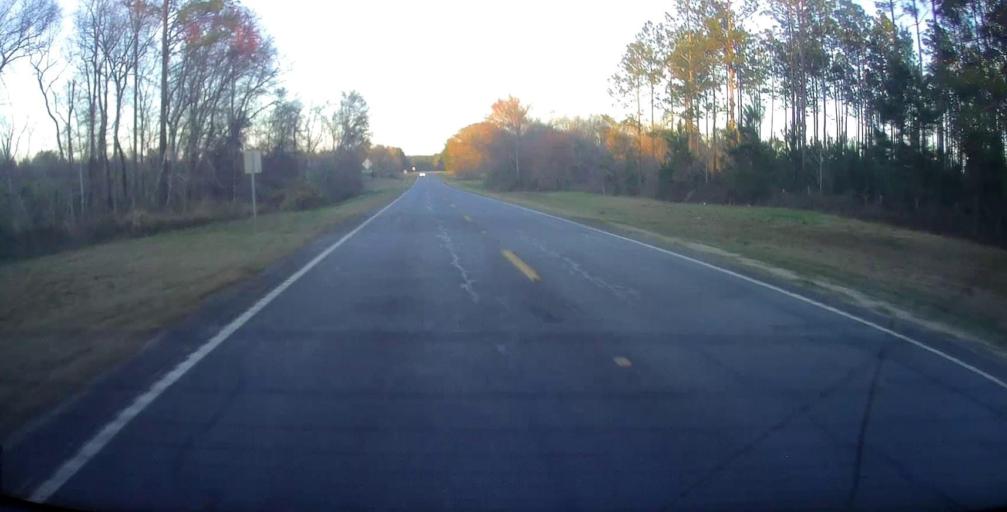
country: US
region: Georgia
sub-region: Dodge County
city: Chester
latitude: 32.2985
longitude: -83.0813
